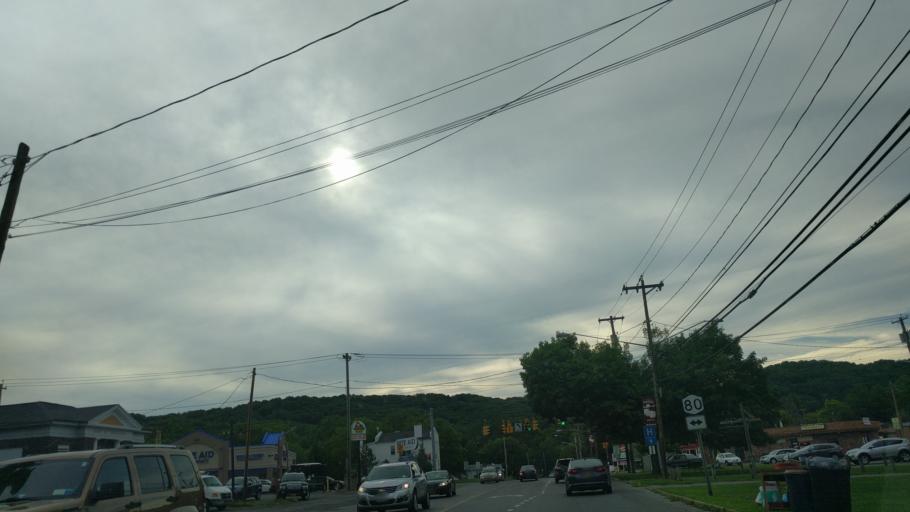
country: US
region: New York
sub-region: Onondaga County
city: Nedrow
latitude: 43.0020
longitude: -76.1522
